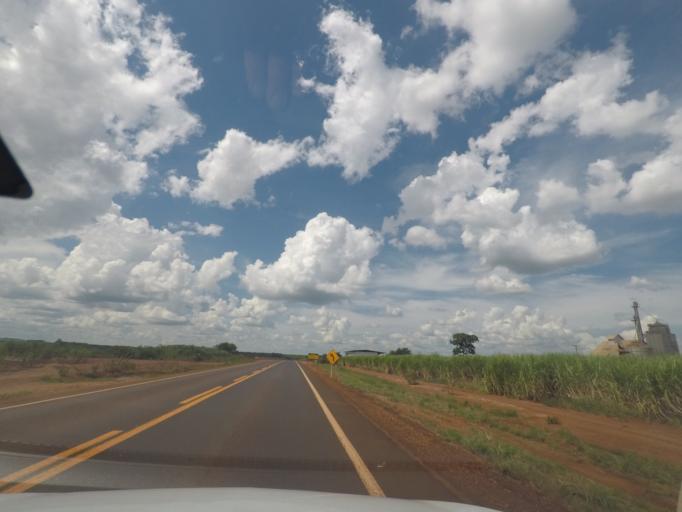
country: BR
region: Minas Gerais
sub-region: Conceicao Das Alagoas
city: Conceicao das Alagoas
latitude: -19.8074
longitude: -48.5817
